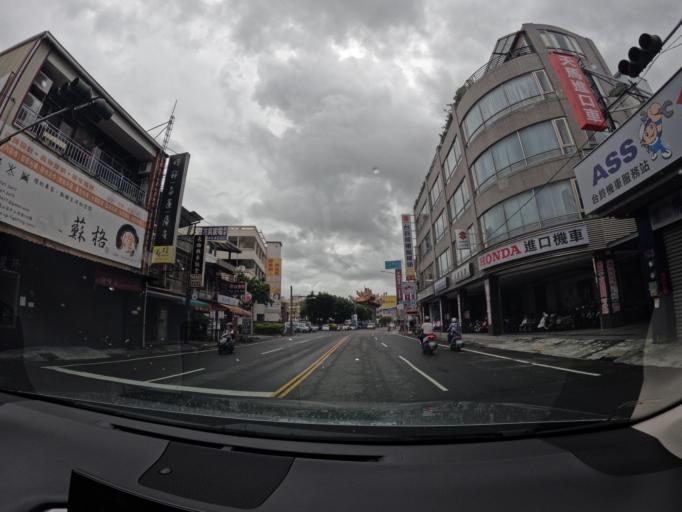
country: TW
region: Taiwan
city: Fengshan
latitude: 22.6275
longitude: 120.3505
